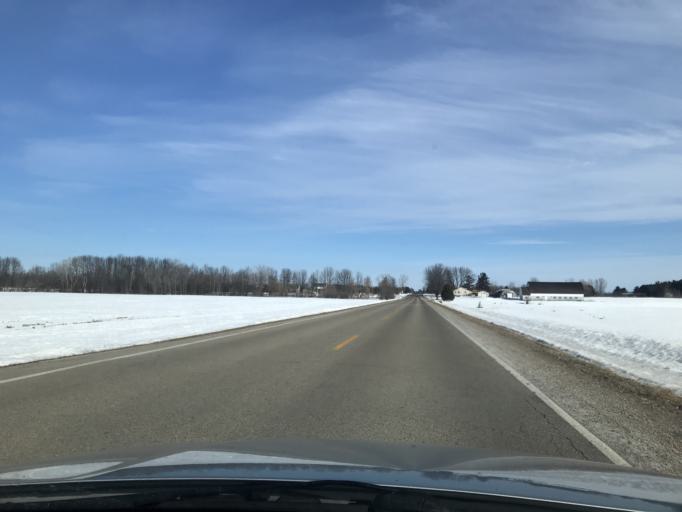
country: US
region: Wisconsin
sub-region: Oconto County
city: Oconto Falls
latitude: 44.8936
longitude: -88.1561
